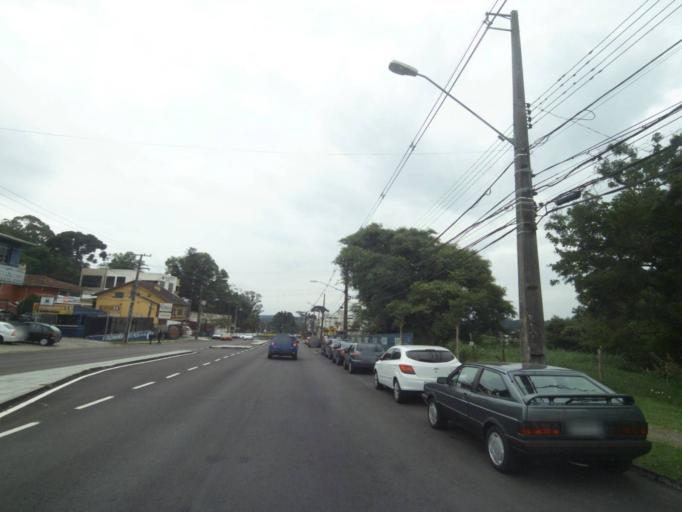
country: BR
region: Parana
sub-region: Curitiba
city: Curitiba
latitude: -25.4160
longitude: -49.2961
